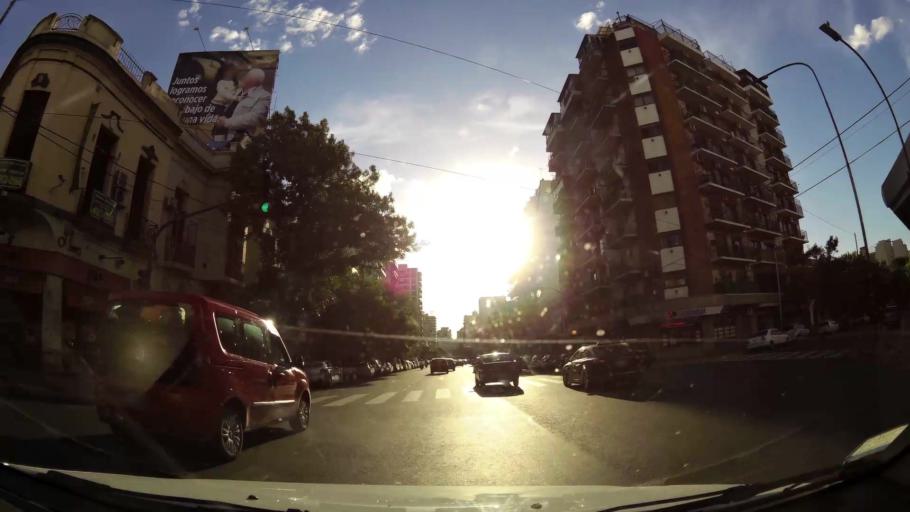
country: AR
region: Buenos Aires F.D.
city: Colegiales
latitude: -34.6058
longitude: -58.4403
